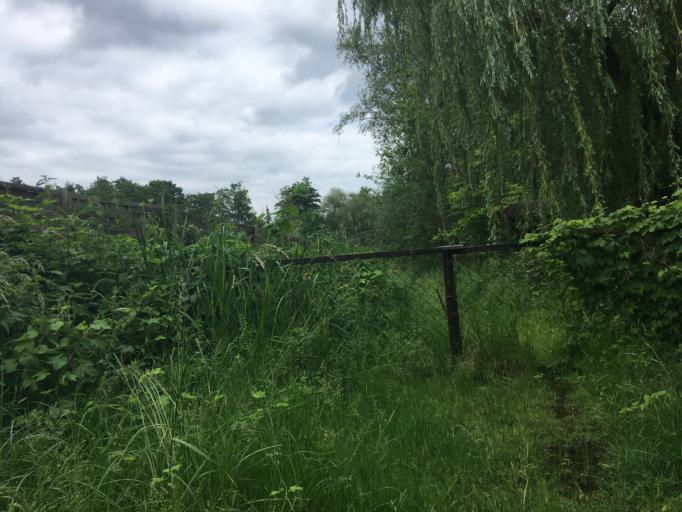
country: DE
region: Berlin
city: Rahnsdorf
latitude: 52.4339
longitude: 13.6902
